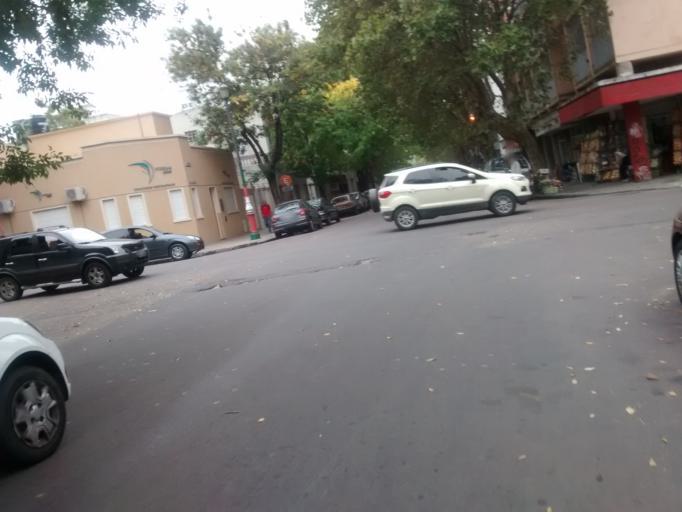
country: AR
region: Buenos Aires
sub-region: Partido de La Plata
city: La Plata
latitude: -34.9221
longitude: -57.9487
